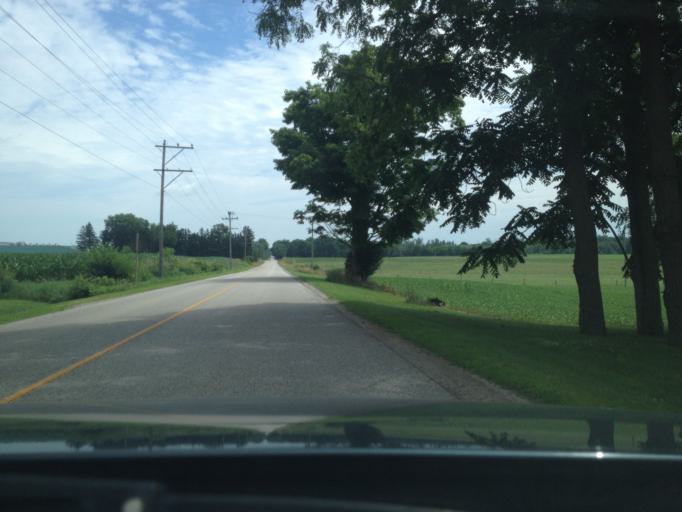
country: CA
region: Ontario
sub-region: Oxford County
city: Woodstock
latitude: 42.9988
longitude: -80.6223
